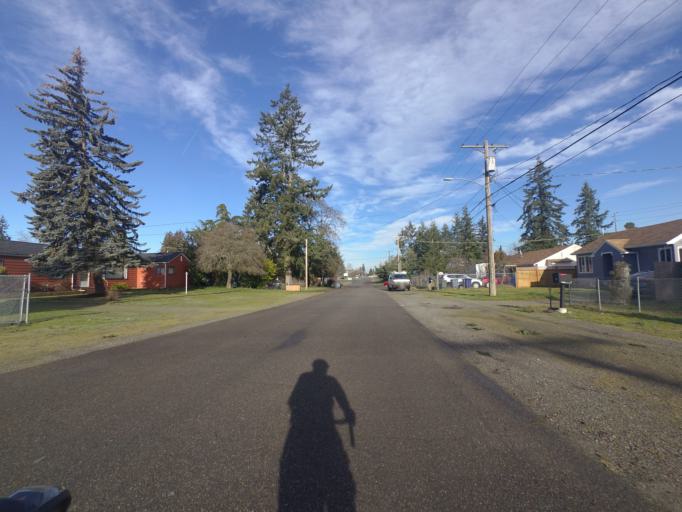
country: US
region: Washington
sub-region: Pierce County
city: McChord Air Force Base
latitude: 47.1567
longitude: -122.4968
